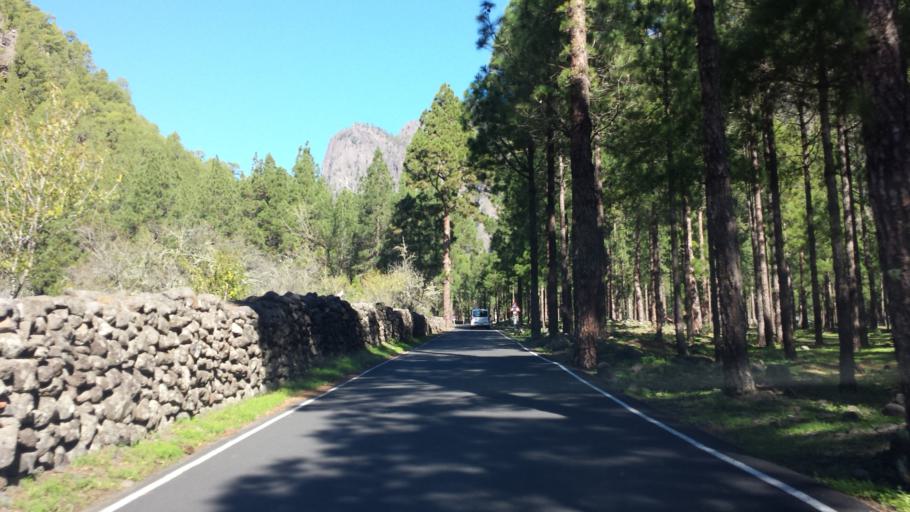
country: ES
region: Canary Islands
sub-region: Provincia de Santa Cruz de Tenerife
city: El Paso
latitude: 28.6755
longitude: -17.8465
